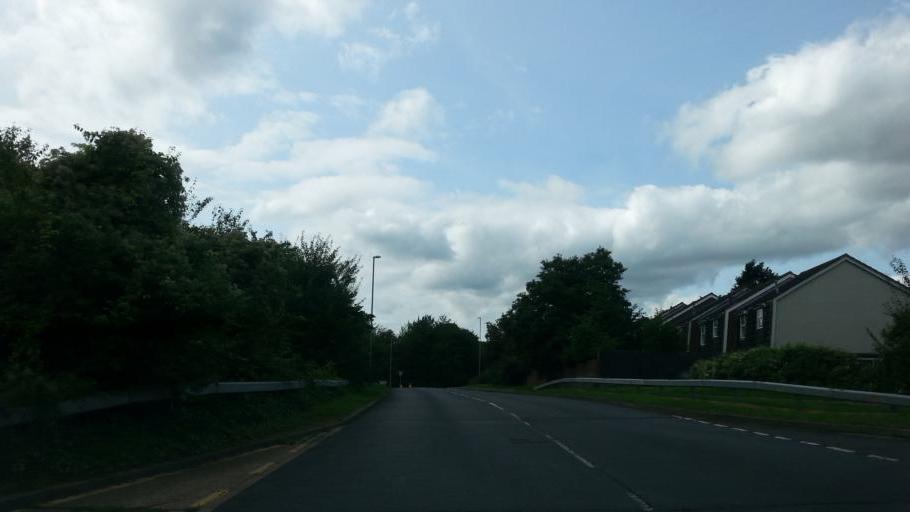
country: GB
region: England
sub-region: Northamptonshire
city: Earls Barton
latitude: 52.2702
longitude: -0.8105
